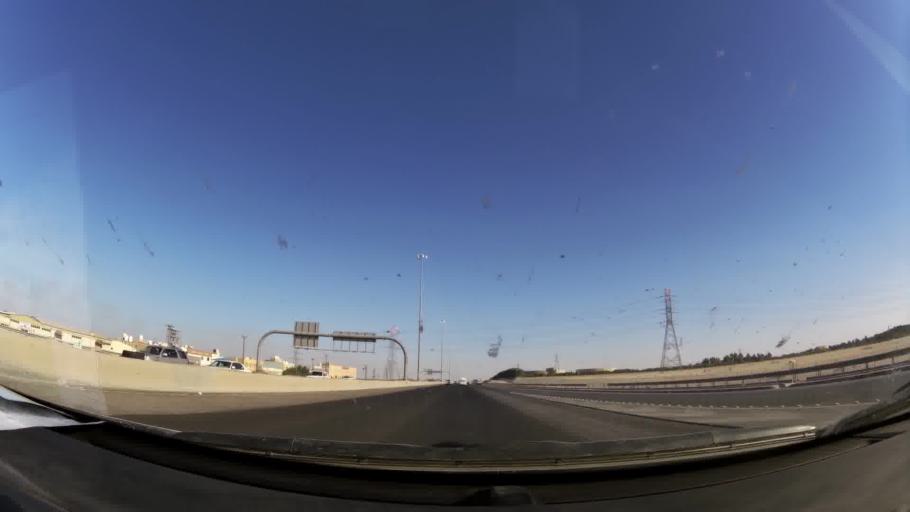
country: KW
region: Muhafazat al Jahra'
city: Al Jahra'
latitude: 29.2941
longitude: 47.7437
